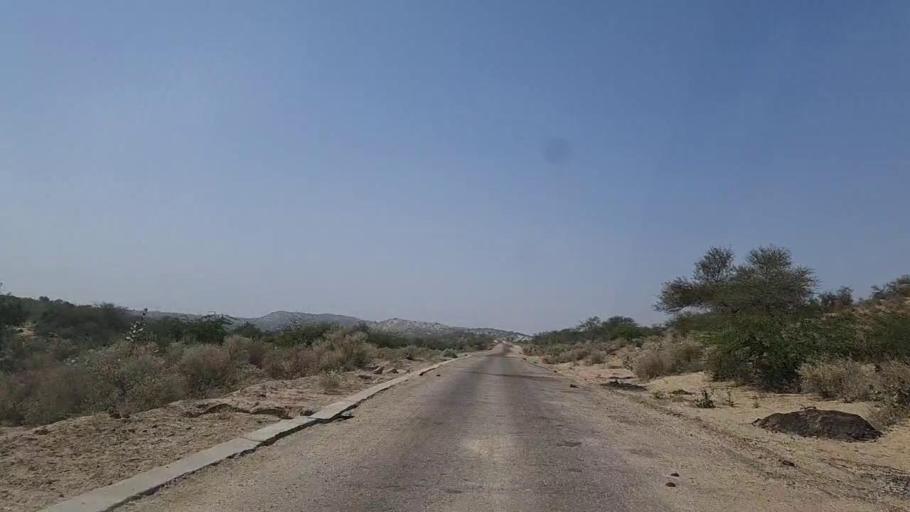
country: PK
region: Sindh
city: Diplo
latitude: 24.5662
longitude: 69.4671
